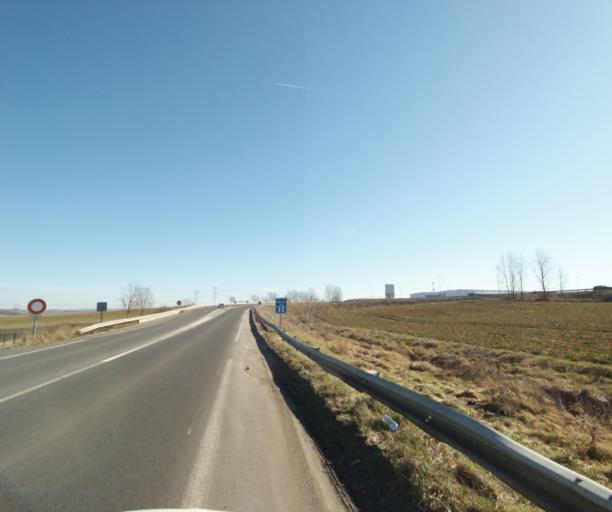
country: FR
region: Lorraine
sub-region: Departement de Meurthe-et-Moselle
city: Fleville-devant-Nancy
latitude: 48.6193
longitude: 6.2084
